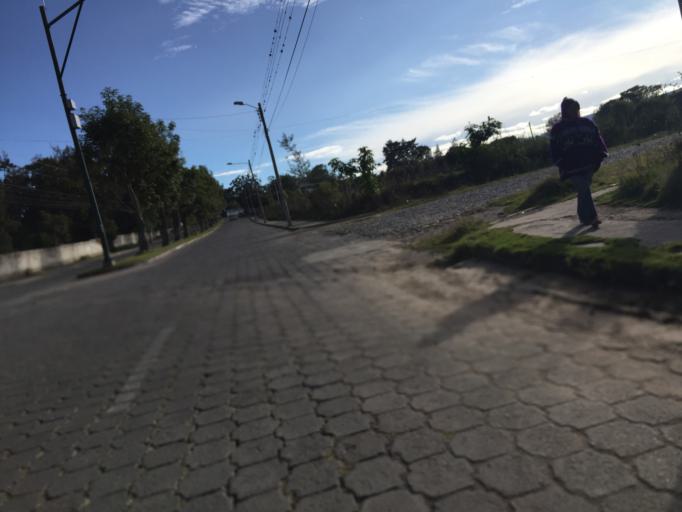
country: EC
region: Imbabura
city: Atuntaqui
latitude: 0.3379
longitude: -78.2082
